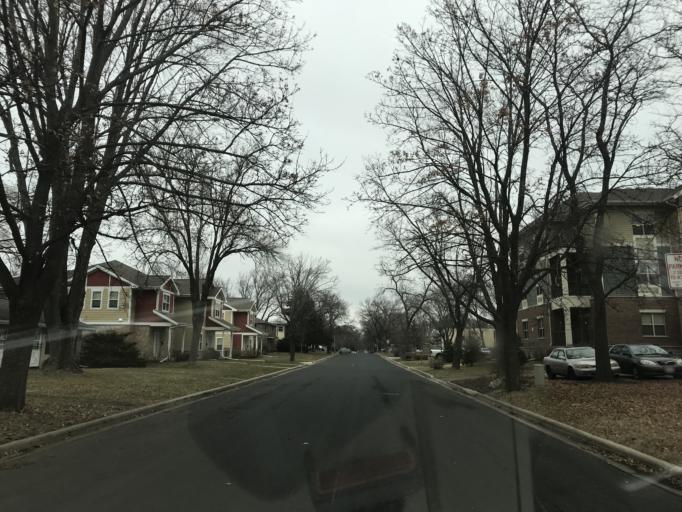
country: US
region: Wisconsin
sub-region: Dane County
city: Monona
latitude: 43.0649
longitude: -89.3272
